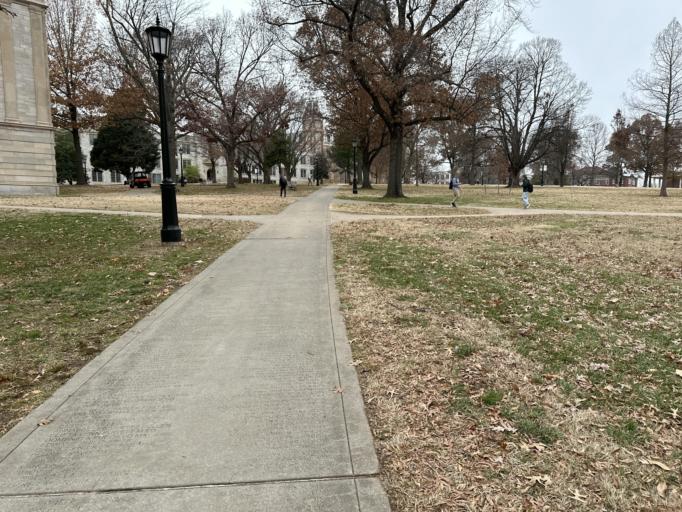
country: US
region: Arkansas
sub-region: Washington County
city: Fayetteville
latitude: 36.0672
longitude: -94.1698
